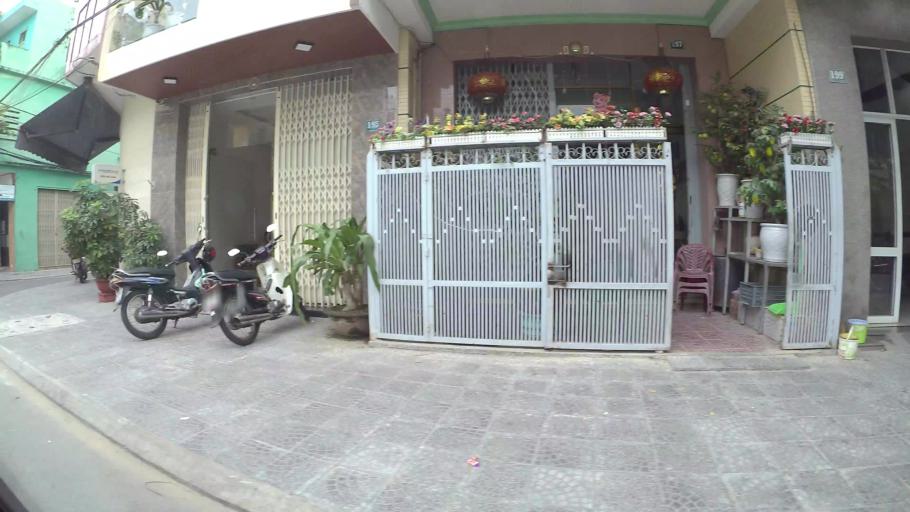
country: VN
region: Da Nang
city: Da Nang
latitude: 16.0573
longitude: 108.2117
